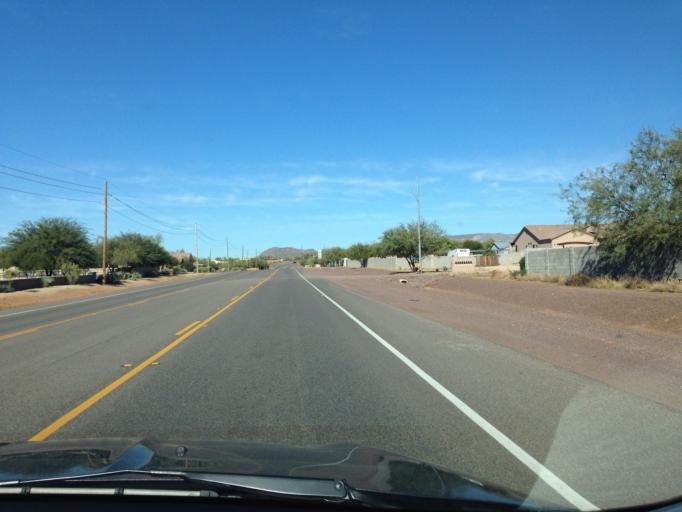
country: US
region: Arizona
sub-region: Maricopa County
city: Anthem
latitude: 33.8356
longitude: -112.0654
